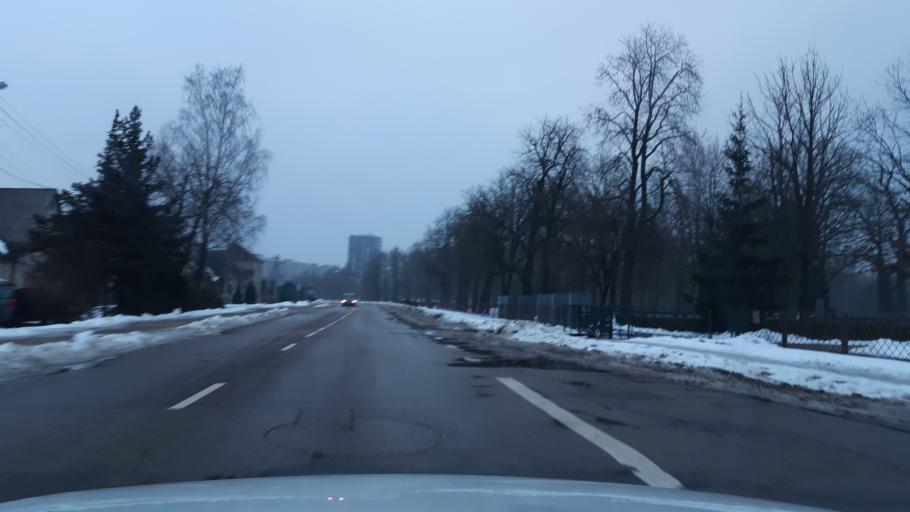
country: LT
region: Kauno apskritis
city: Dainava (Kaunas)
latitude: 54.8790
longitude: 23.9490
